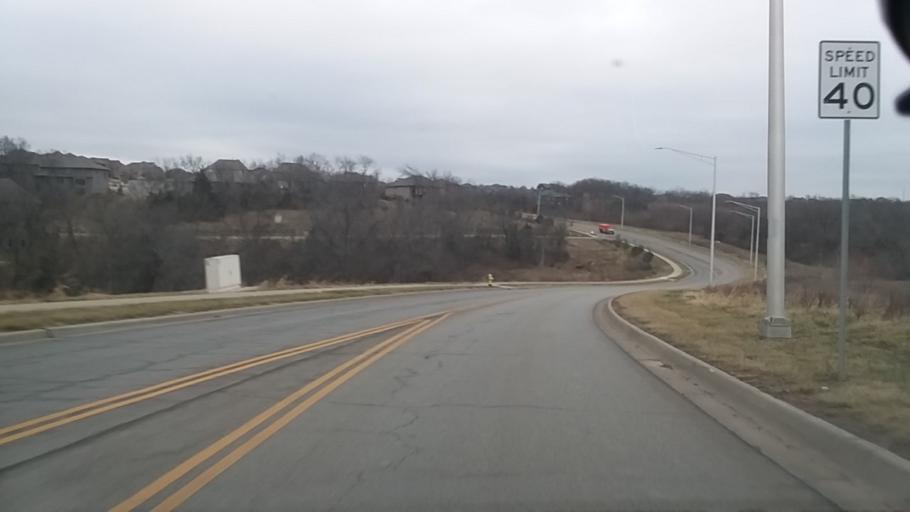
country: US
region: Kansas
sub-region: Johnson County
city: Olathe
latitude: 38.9019
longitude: -94.8684
